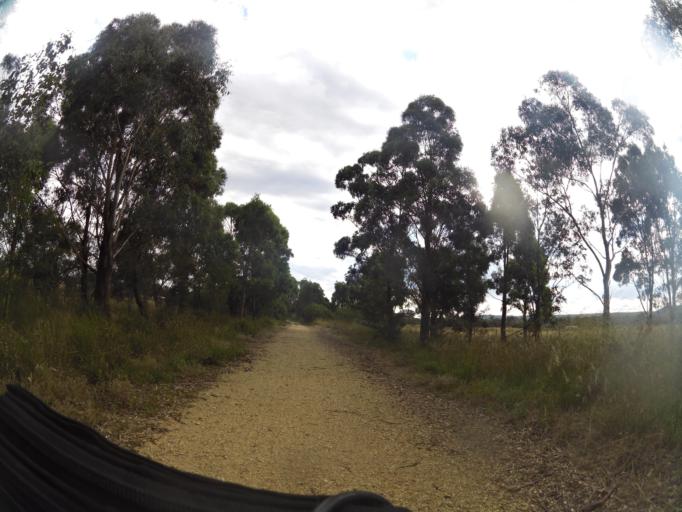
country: AU
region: Victoria
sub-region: Latrobe
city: Traralgon
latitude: -38.0509
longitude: 146.6301
